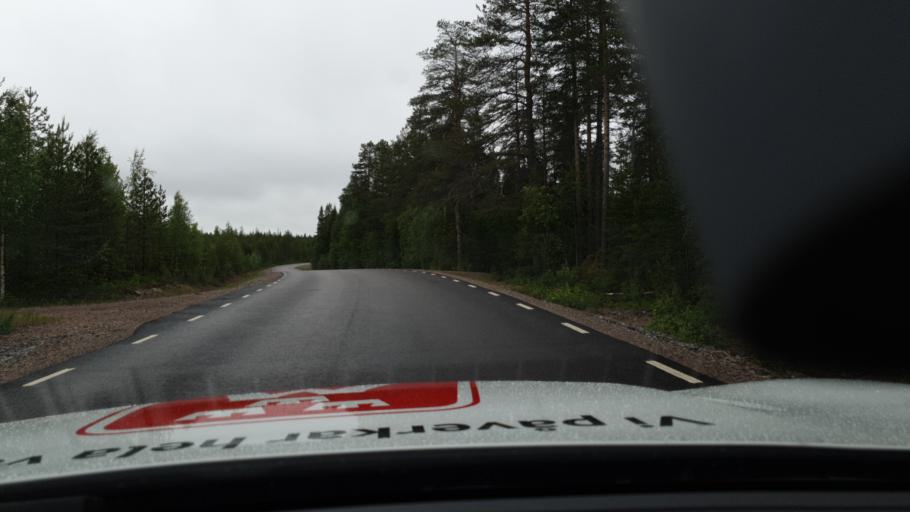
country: SE
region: Norrbotten
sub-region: Overtornea Kommun
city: OEvertornea
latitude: 66.4322
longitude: 23.5193
